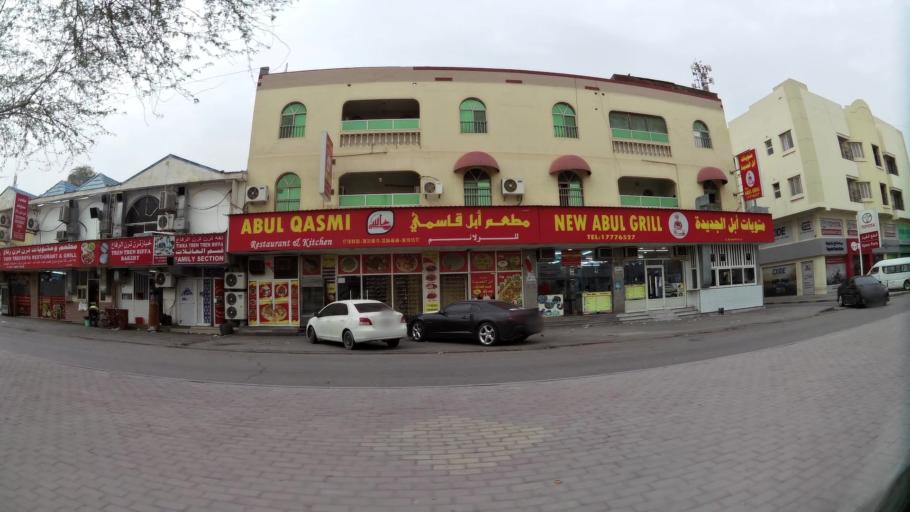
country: BH
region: Northern
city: Ar Rifa'
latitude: 26.1154
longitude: 50.5755
